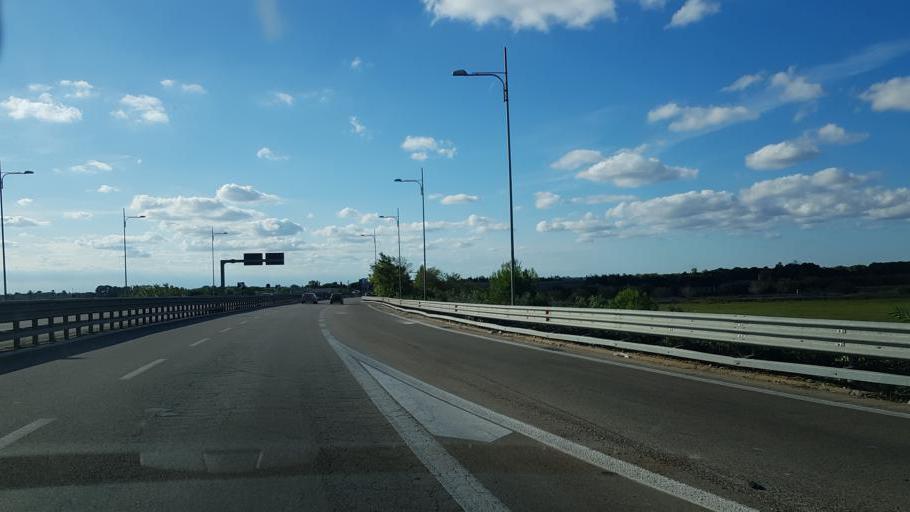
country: IT
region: Apulia
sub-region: Provincia di Lecce
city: Lequile
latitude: 40.3264
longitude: 18.1472
